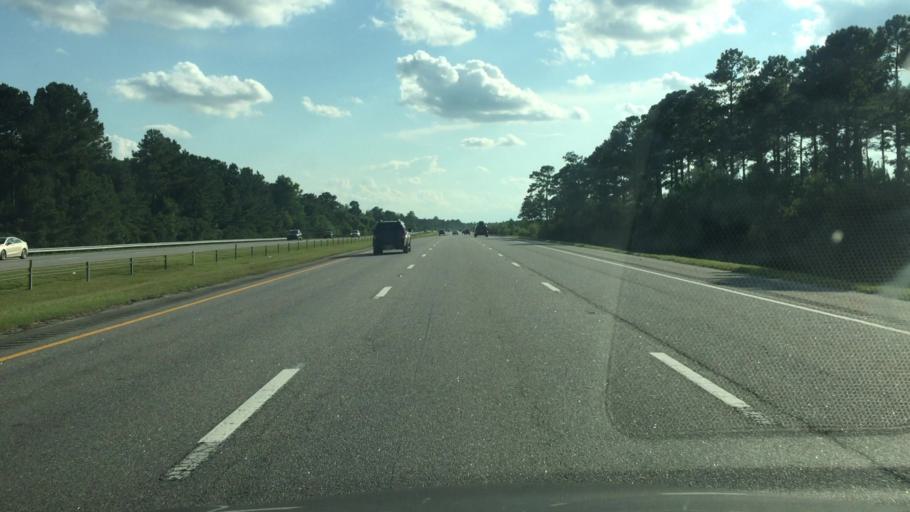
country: US
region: South Carolina
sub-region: Horry County
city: Myrtle Beach
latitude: 33.7775
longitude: -78.8131
